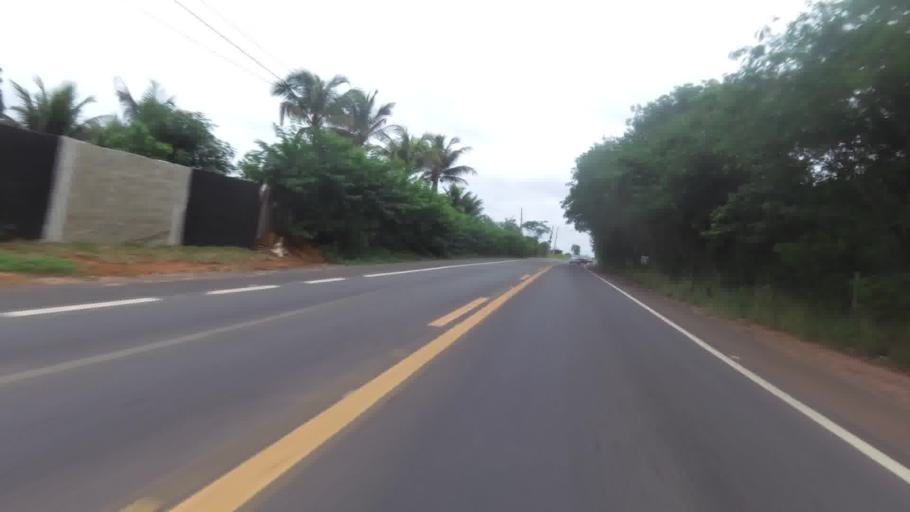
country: BR
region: Espirito Santo
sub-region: Piuma
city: Piuma
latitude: -20.8079
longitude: -40.6786
